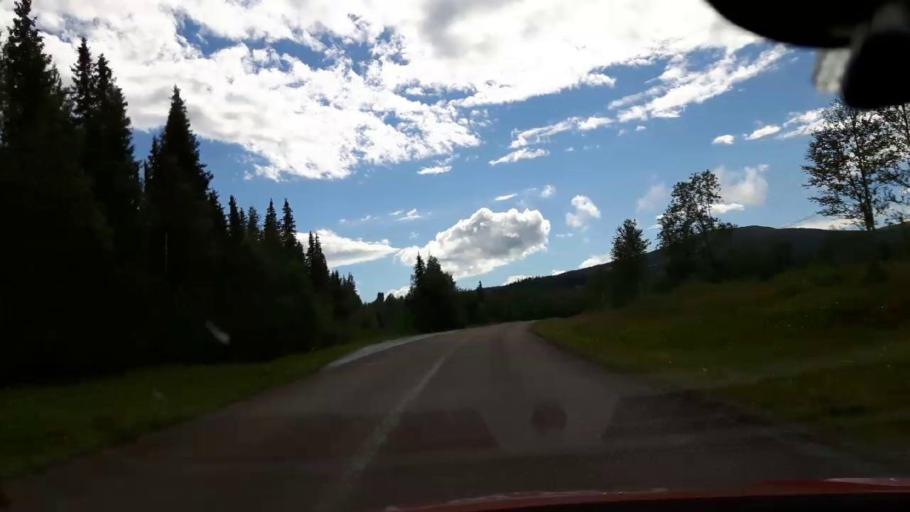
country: SE
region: Jaemtland
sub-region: Are Kommun
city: Are
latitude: 63.3066
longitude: 13.2258
